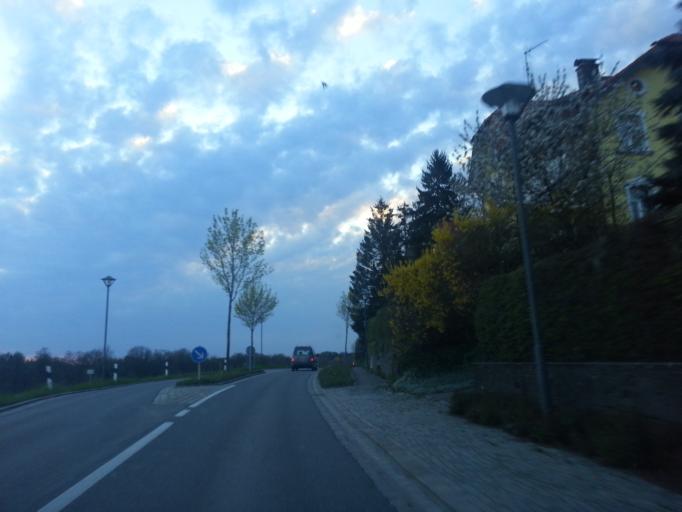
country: DE
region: Bavaria
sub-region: Swabia
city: Bodolz
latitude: 47.5660
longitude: 9.6631
